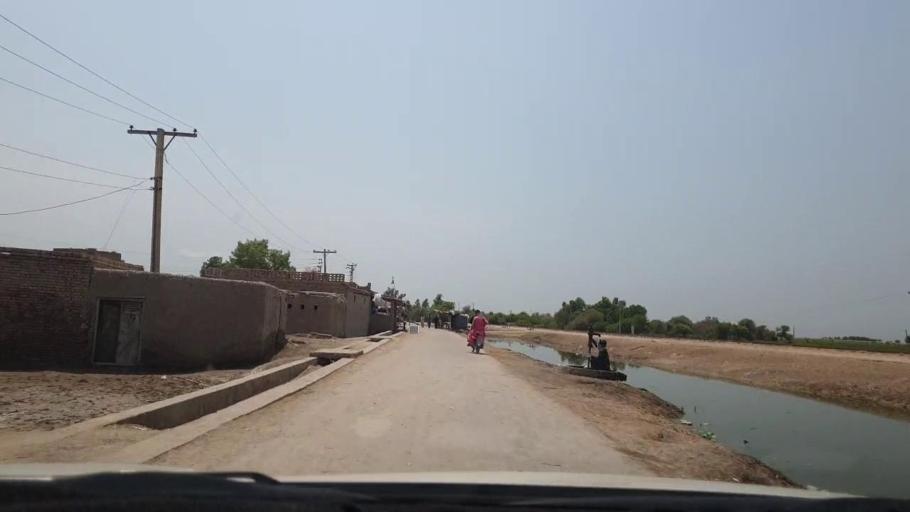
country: PK
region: Sindh
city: Radhan
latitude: 27.2450
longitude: 67.9876
